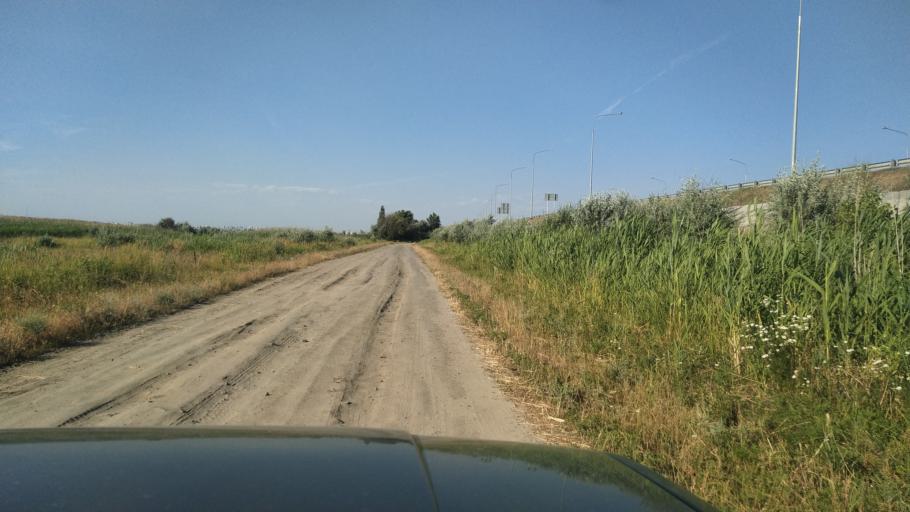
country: RU
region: Rostov
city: Bataysk
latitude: 47.1222
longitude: 39.6607
